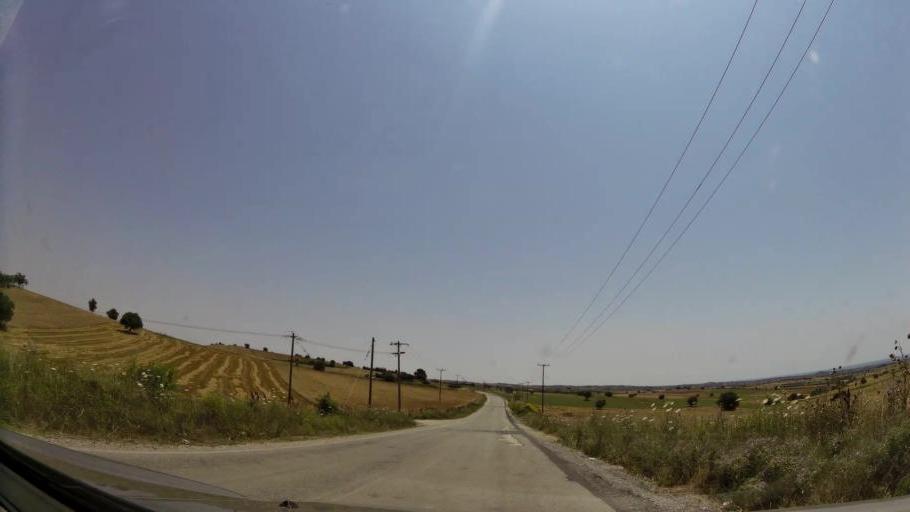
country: GR
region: Central Macedonia
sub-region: Nomos Thessalonikis
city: Neoi Epivates
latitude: 40.4657
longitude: 22.9026
